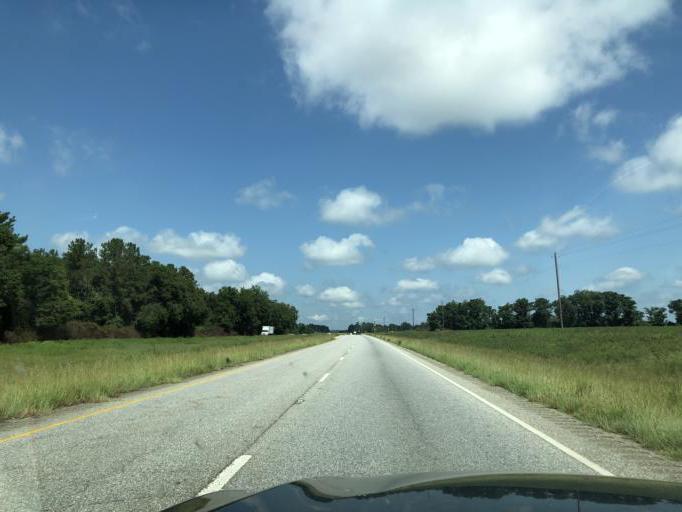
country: US
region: Alabama
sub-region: Henry County
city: Abbeville
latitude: 31.6085
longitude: -85.2770
